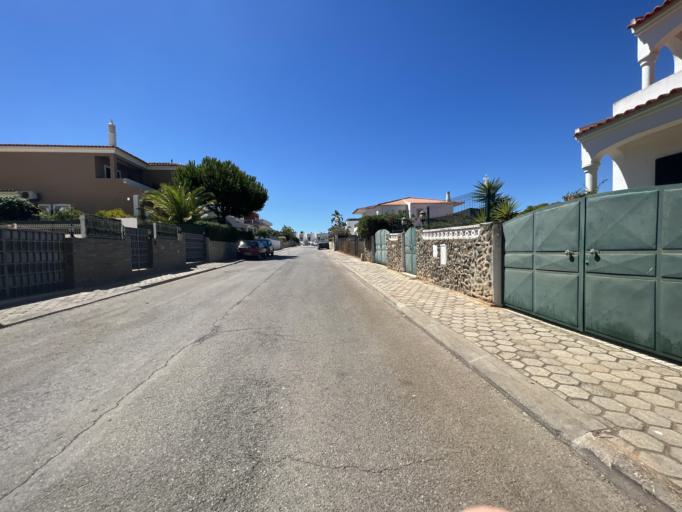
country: PT
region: Faro
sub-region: Portimao
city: Portimao
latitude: 37.1298
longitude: -8.5205
